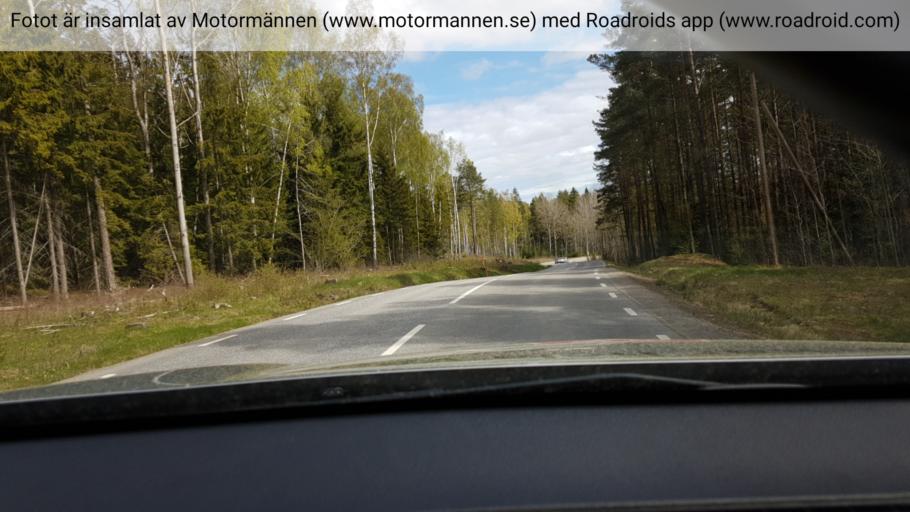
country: SE
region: Stockholm
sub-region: Haninge Kommun
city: Haninge
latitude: 59.1654
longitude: 18.1745
